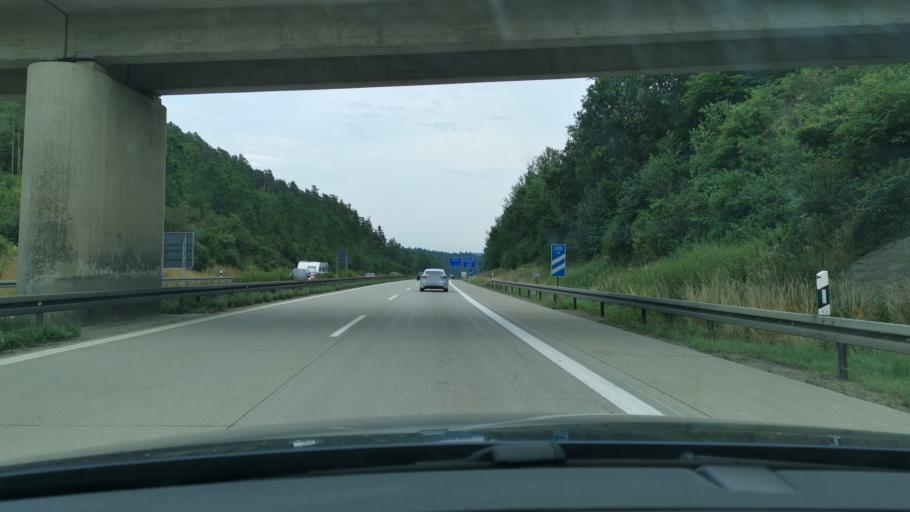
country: DE
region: Bavaria
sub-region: Upper Palatinate
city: Wernberg-Koblitz
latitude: 49.5250
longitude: 12.1544
